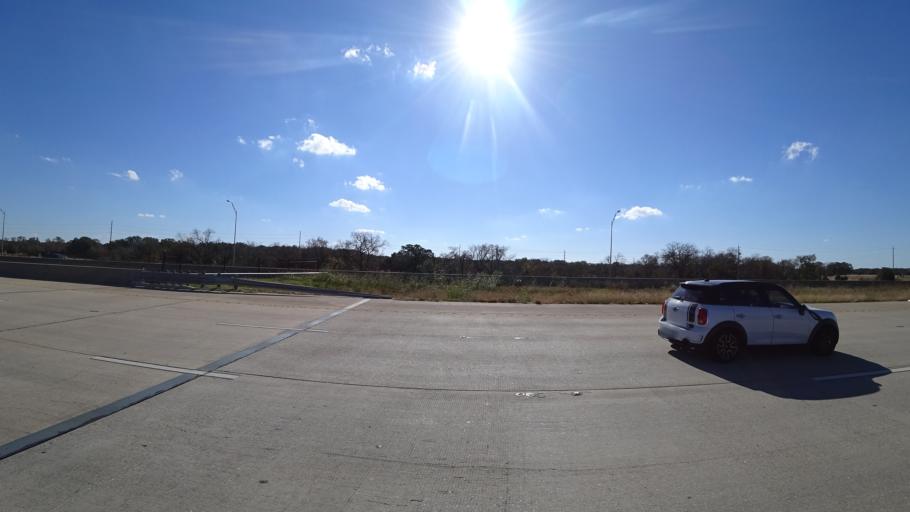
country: US
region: Texas
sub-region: Williamson County
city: Brushy Creek
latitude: 30.4793
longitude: -97.7344
